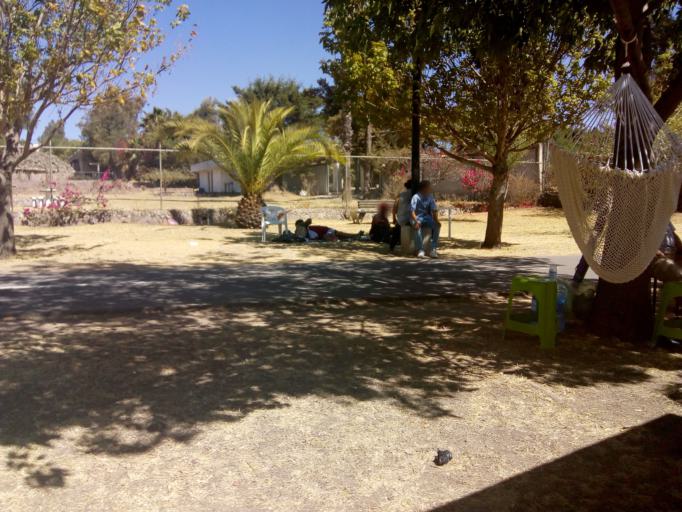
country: MX
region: Guanajuato
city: Leon
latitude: 21.1786
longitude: -101.6790
